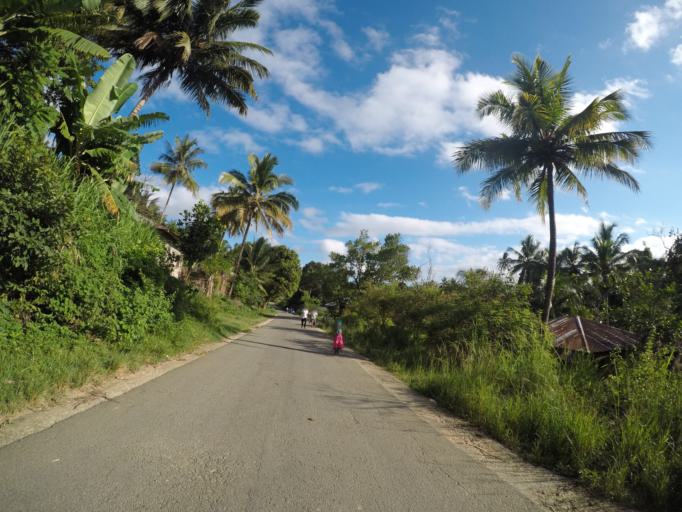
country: TZ
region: Pemba South
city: Mtambile
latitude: -5.3579
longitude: 39.7099
